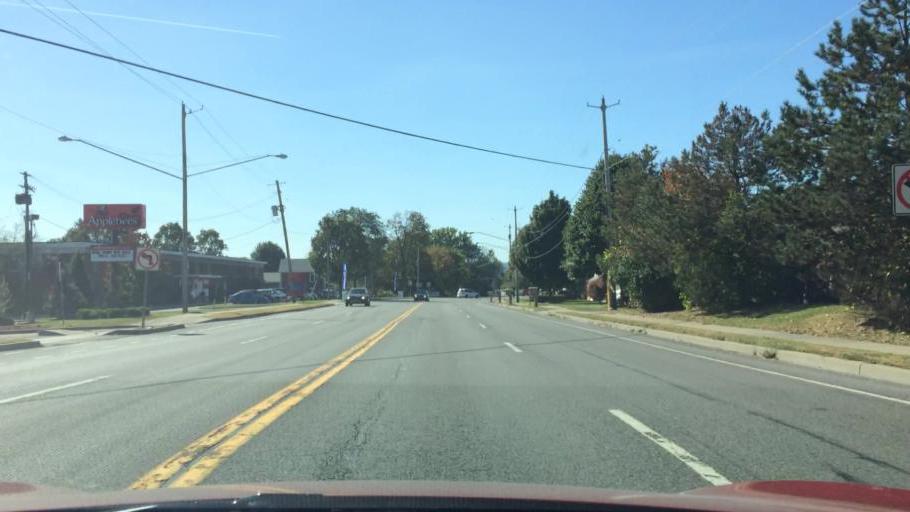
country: US
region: New York
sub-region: Broome County
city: Port Dickinson
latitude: 42.1302
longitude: -75.9060
